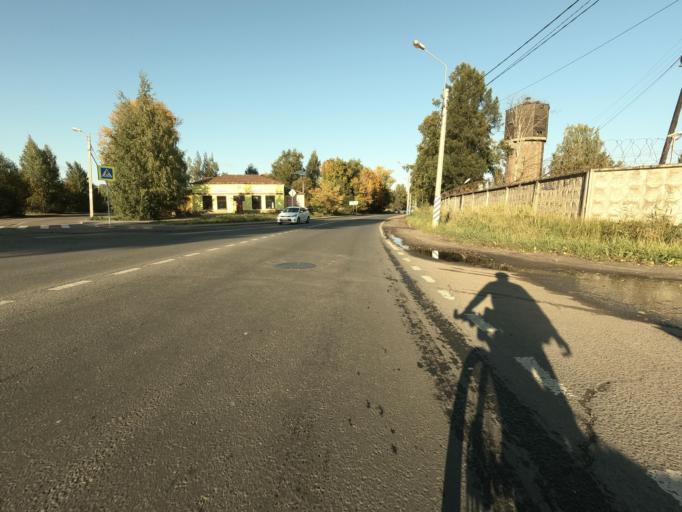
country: RU
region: St.-Petersburg
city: Pontonnyy
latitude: 59.7572
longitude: 30.6181
